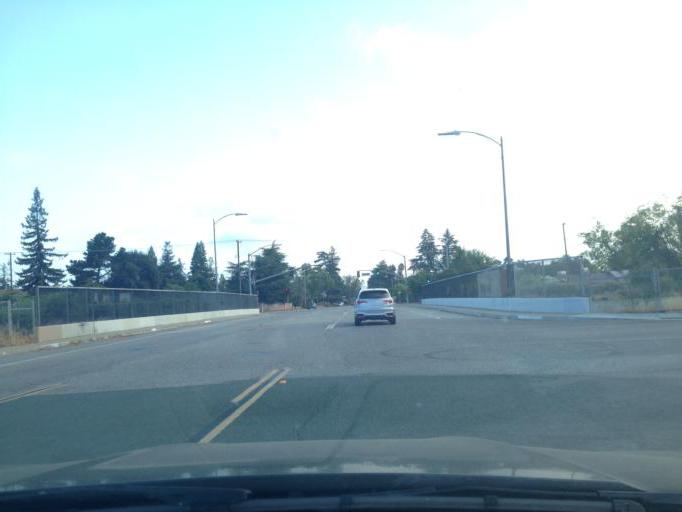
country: US
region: California
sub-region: Santa Clara County
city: Cambrian Park
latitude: 37.2499
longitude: -121.9222
